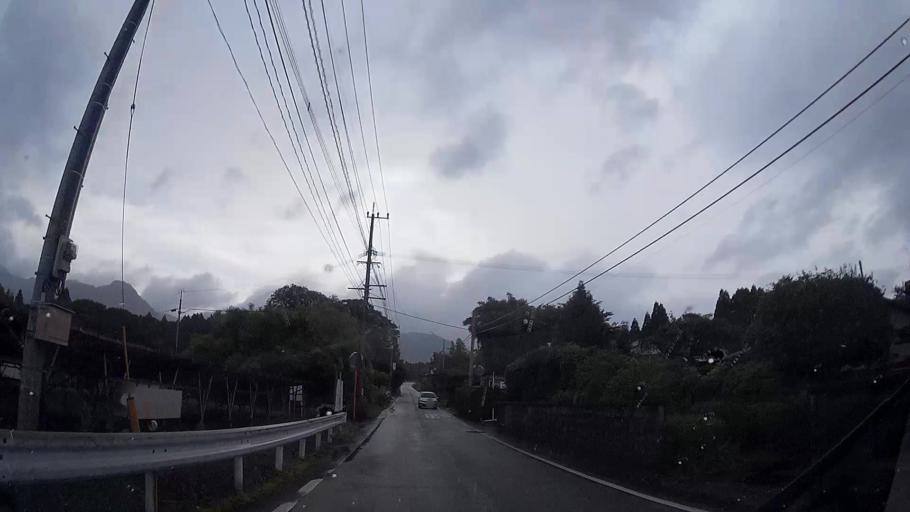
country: JP
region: Kumamoto
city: Aso
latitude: 32.8453
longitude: 131.0208
